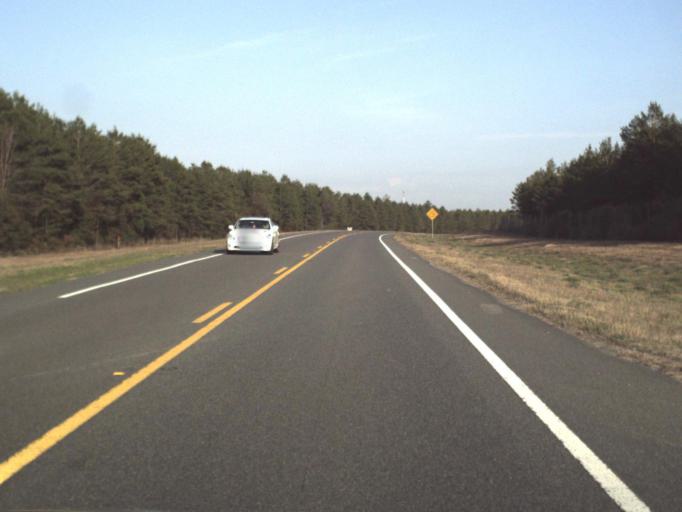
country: US
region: Florida
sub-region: Bay County
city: Lynn Haven
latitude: 30.4389
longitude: -85.7062
